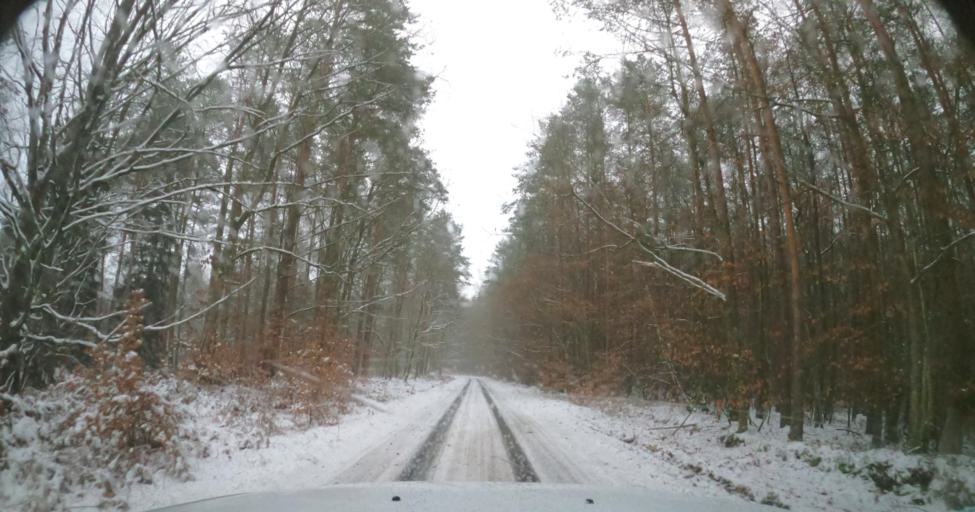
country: PL
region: West Pomeranian Voivodeship
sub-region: Powiat goleniowski
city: Przybiernow
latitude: 53.6632
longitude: 14.7643
